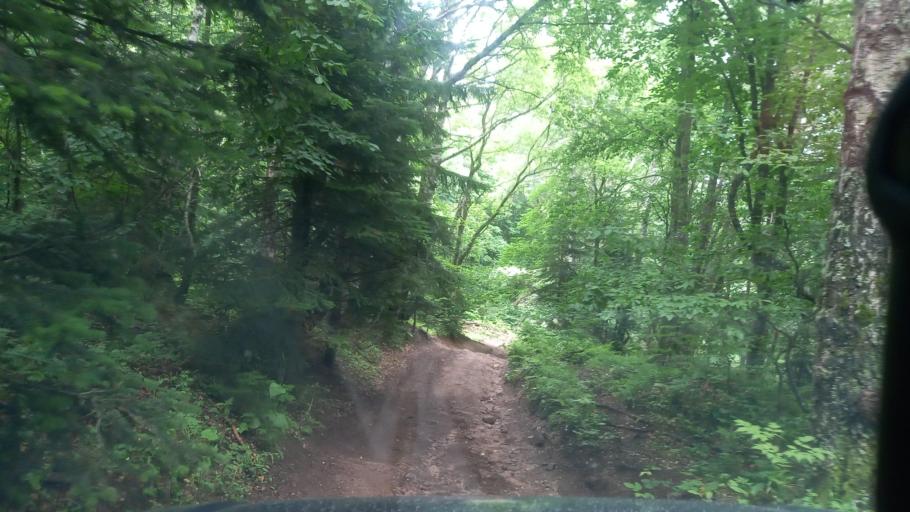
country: RU
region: Karachayevo-Cherkesiya
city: Kurdzhinovo
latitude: 43.8065
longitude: 40.8517
